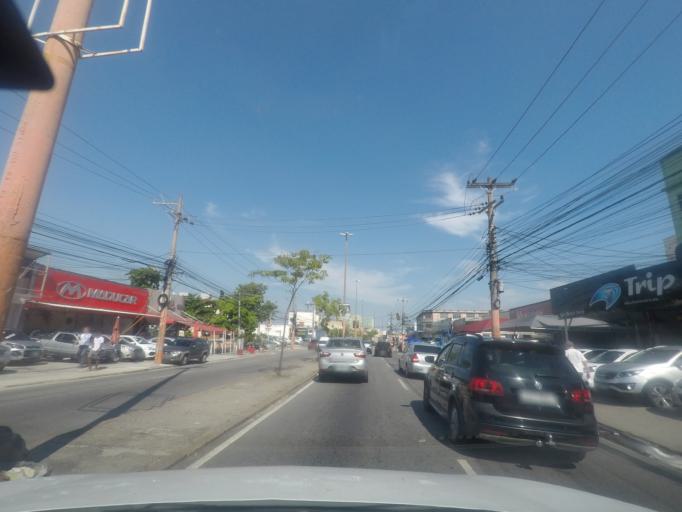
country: BR
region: Rio de Janeiro
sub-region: Sao Joao De Meriti
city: Sao Joao de Meriti
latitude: -22.8781
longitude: -43.3601
